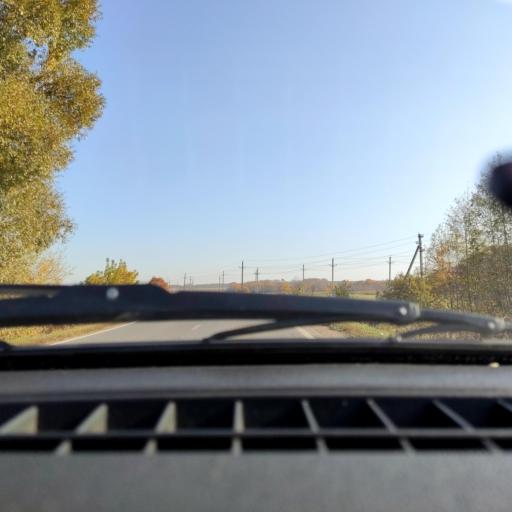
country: RU
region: Bashkortostan
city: Iglino
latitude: 54.7433
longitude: 56.2185
